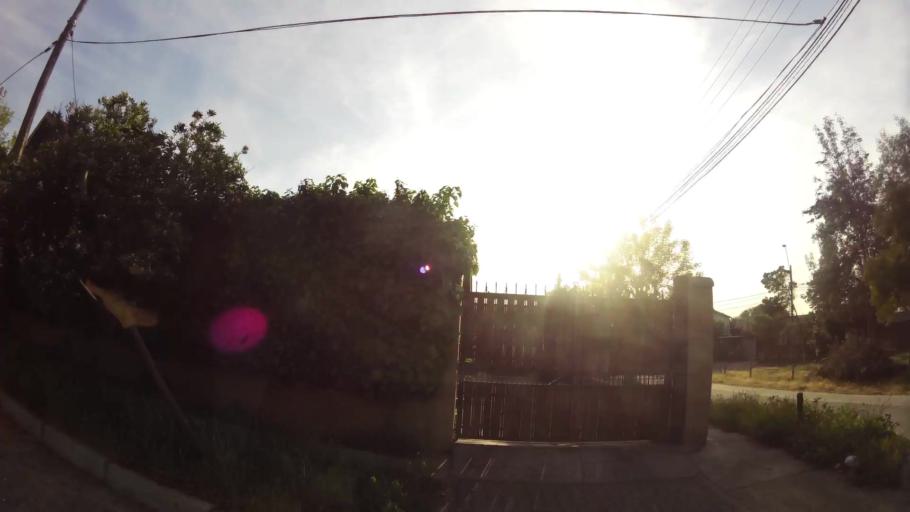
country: CL
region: Santiago Metropolitan
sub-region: Provincia de Maipo
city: San Bernardo
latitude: -33.5275
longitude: -70.6751
